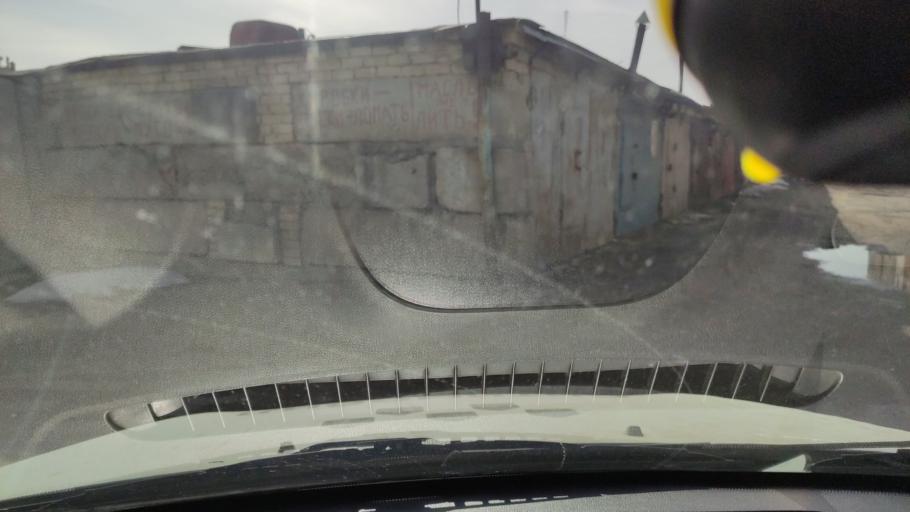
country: RU
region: Samara
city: Zhigulevsk
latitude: 53.4908
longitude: 49.4810
